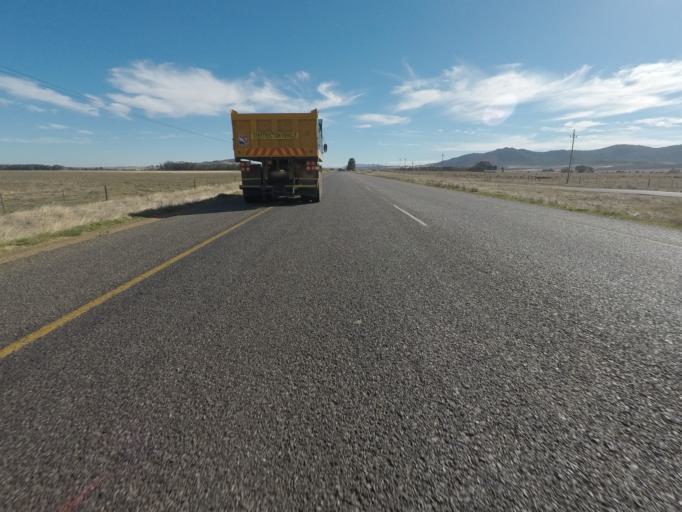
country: ZA
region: Western Cape
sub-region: West Coast District Municipality
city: Malmesbury
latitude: -33.6266
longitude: 18.7239
